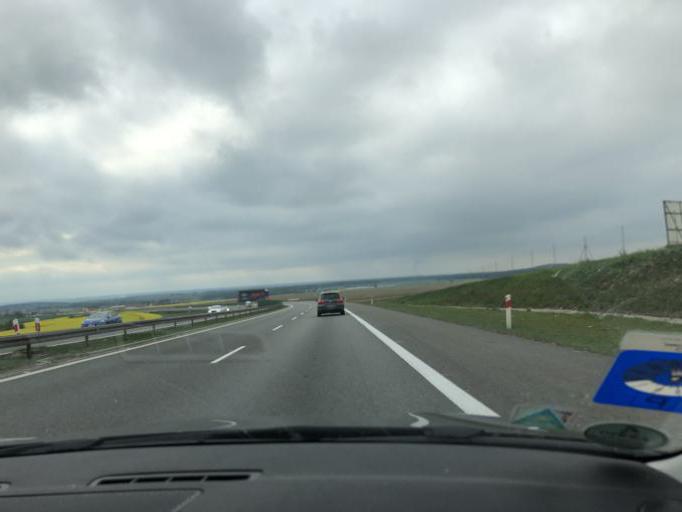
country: PL
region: Opole Voivodeship
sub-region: Powiat krapkowicki
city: Rozwadza
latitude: 50.4811
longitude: 18.1201
